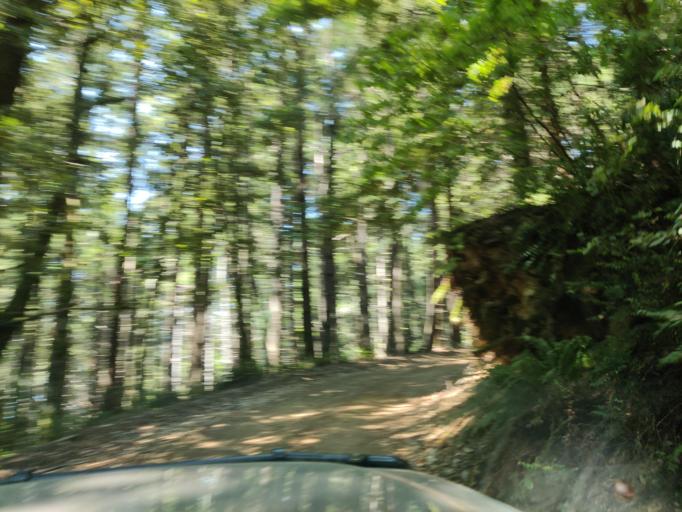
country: US
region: California
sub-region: Humboldt County
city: Redway
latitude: 39.9601
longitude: -123.9588
